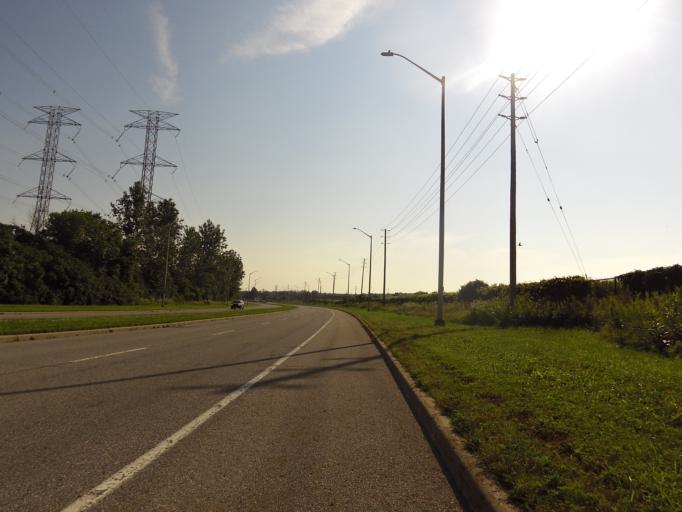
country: CA
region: Ontario
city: Bells Corners
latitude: 45.3265
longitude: -75.7544
